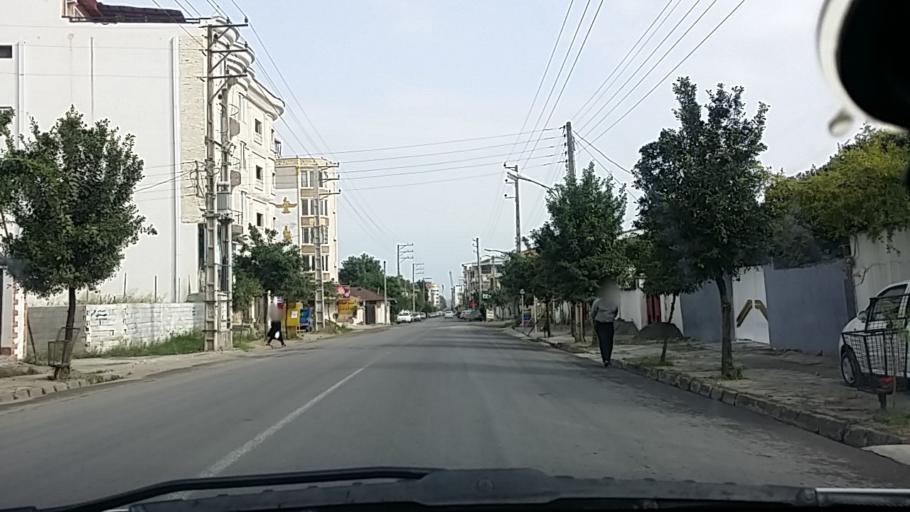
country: IR
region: Mazandaran
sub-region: Nowshahr
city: Nowshahr
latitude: 36.6422
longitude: 51.5083
